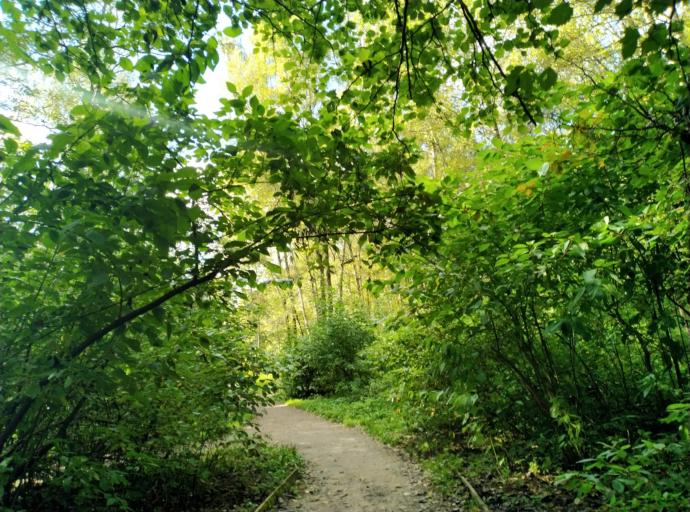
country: RU
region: Moscow
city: Khimki
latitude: 55.8657
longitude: 37.4190
